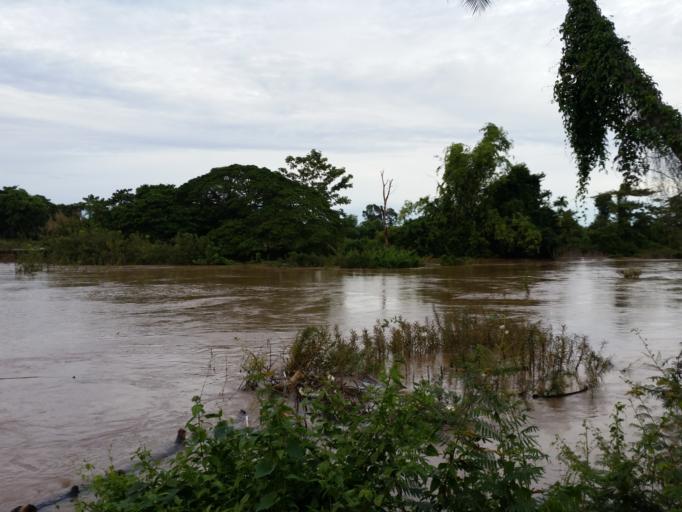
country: LA
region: Champasak
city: Khong
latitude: 13.9622
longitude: 105.9335
